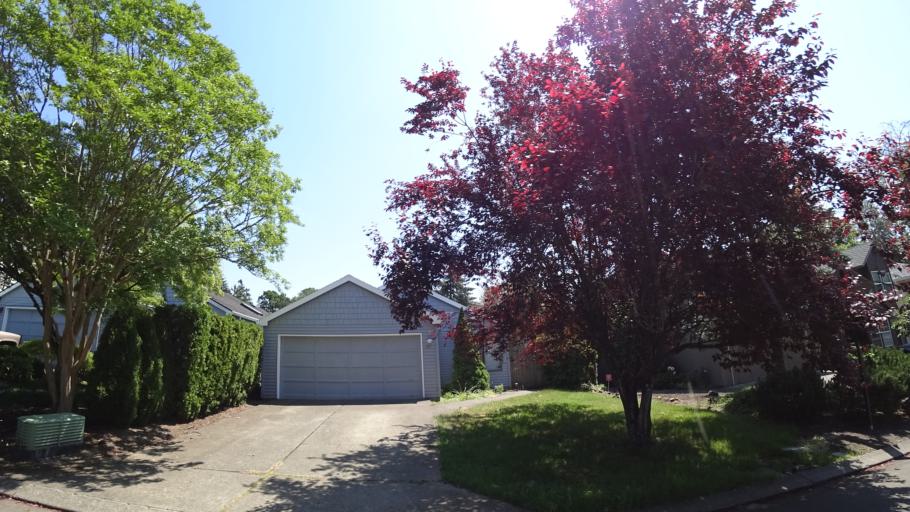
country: US
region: Oregon
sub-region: Washington County
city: Metzger
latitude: 45.4289
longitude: -122.7295
